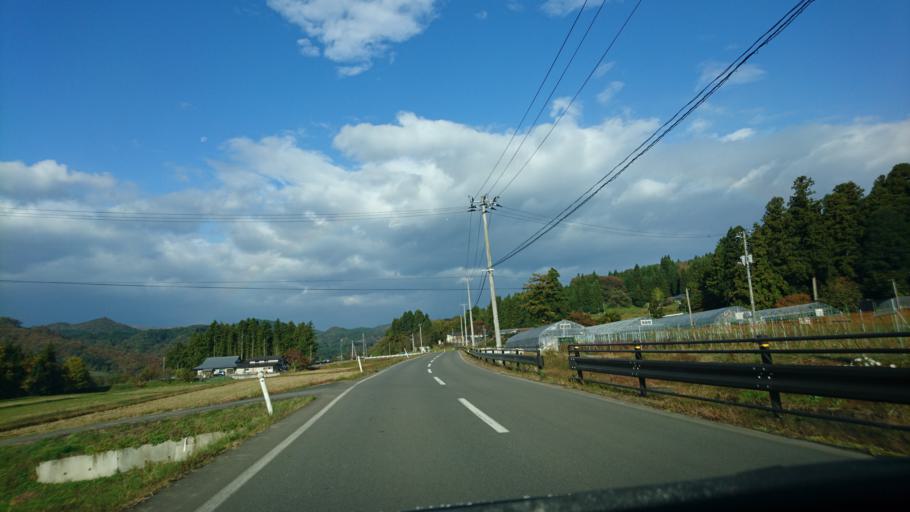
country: JP
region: Iwate
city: Mizusawa
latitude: 39.0455
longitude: 141.0570
